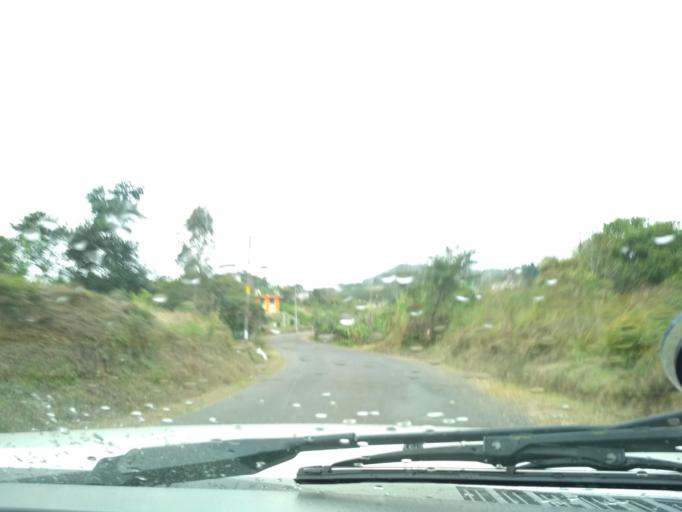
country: MX
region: Veracruz
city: El Castillo
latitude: 19.5348
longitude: -96.8160
